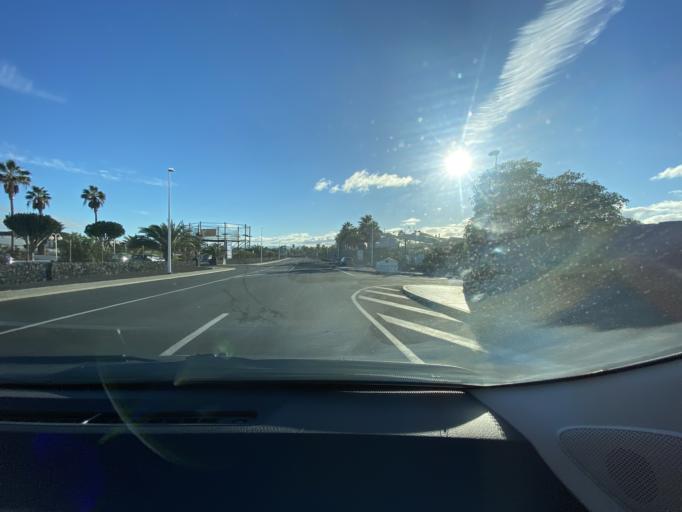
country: ES
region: Canary Islands
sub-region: Provincia de Las Palmas
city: Playa Blanca
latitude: 28.8635
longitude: -13.8420
